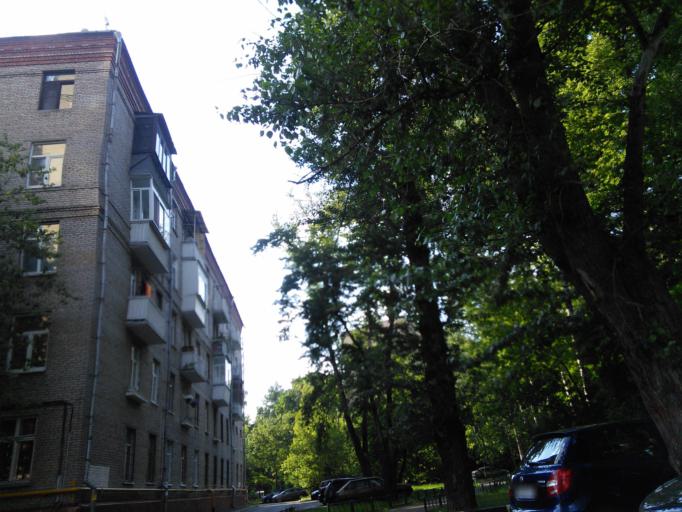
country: RU
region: Moskovskaya
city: Bogorodskoye
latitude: 55.8131
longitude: 37.7172
